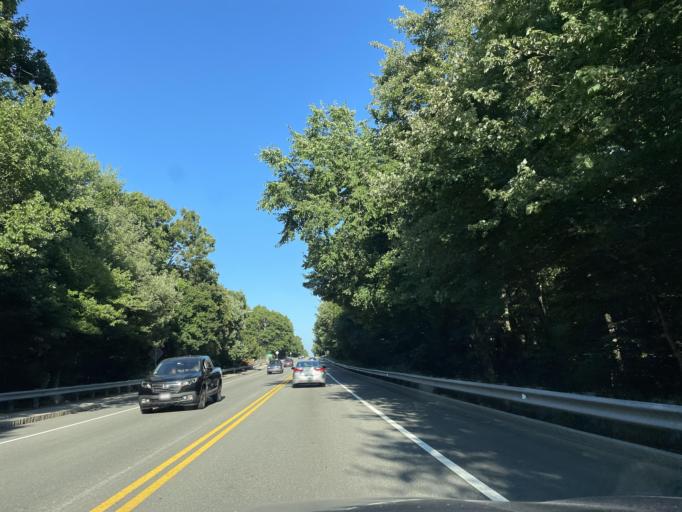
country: US
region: Massachusetts
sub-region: Bristol County
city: Mansfield Center
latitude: 42.0282
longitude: -71.1774
